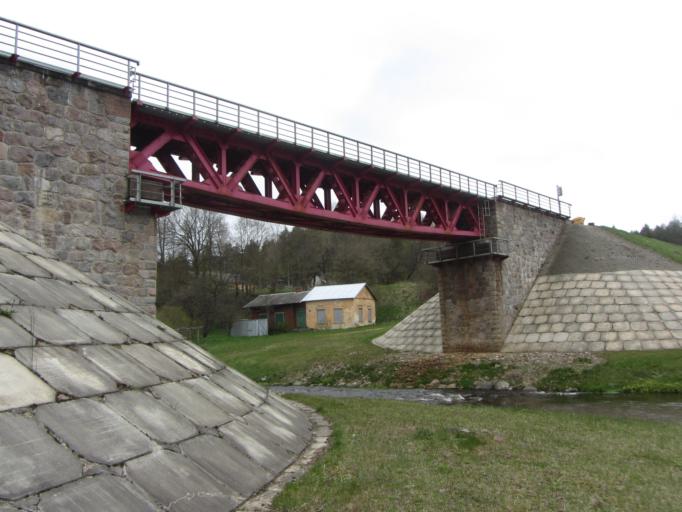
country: LT
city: Salcininkai
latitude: 54.4385
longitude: 25.2863
